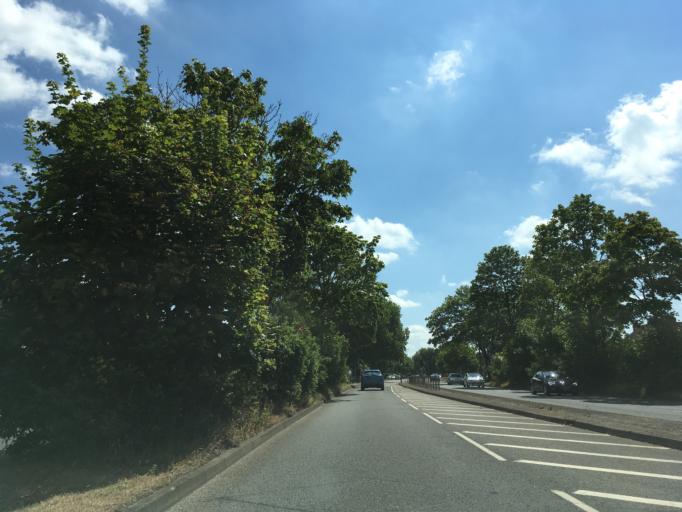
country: GB
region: England
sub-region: Gloucestershire
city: Gloucester
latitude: 51.8756
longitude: -2.2359
